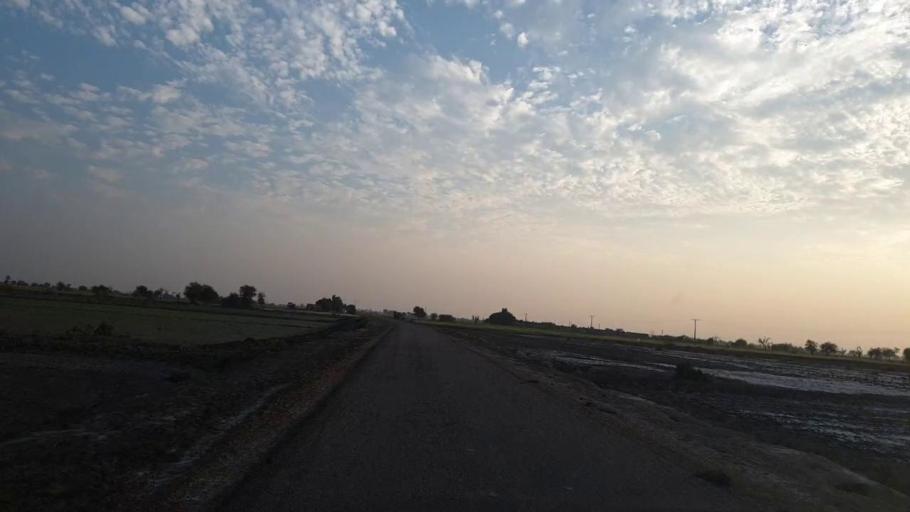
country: PK
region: Sindh
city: Pithoro
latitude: 25.5900
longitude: 69.3051
